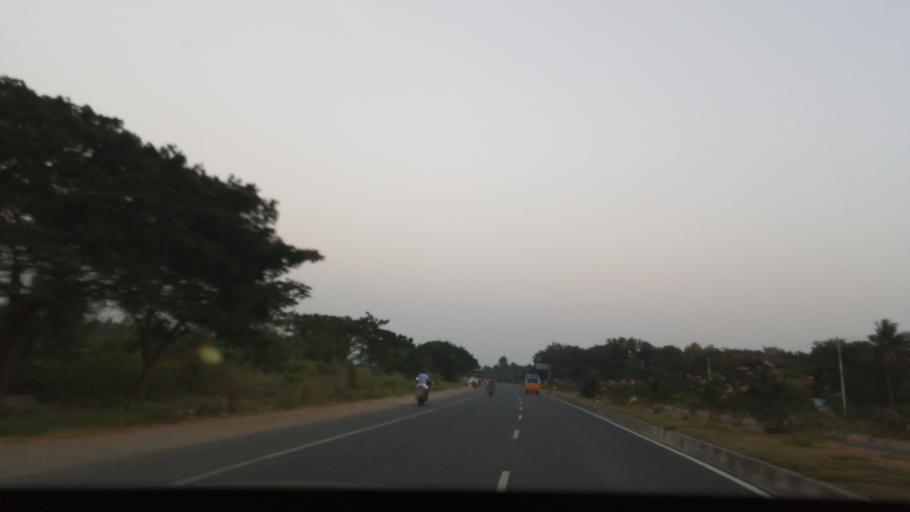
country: IN
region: Tamil Nadu
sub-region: Salem
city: Belur
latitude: 11.6567
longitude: 78.3377
